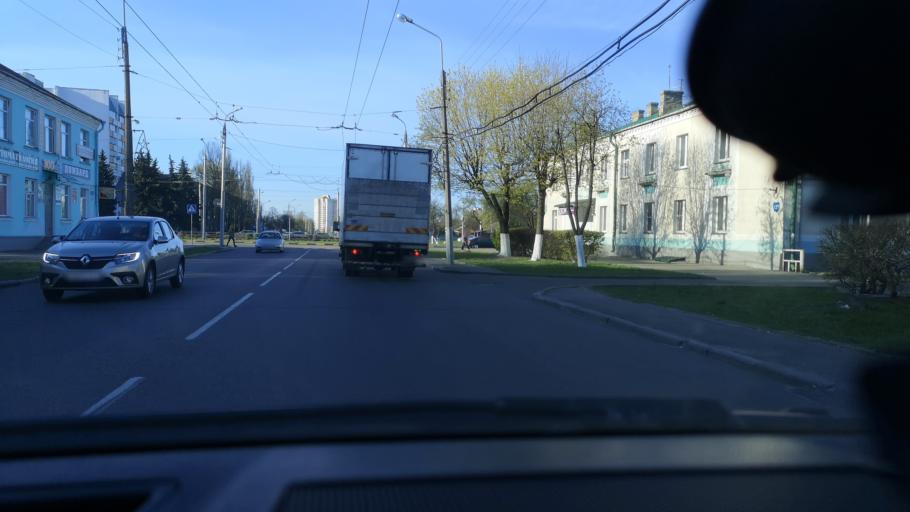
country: BY
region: Gomel
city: Gomel
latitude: 52.4198
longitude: 30.9726
